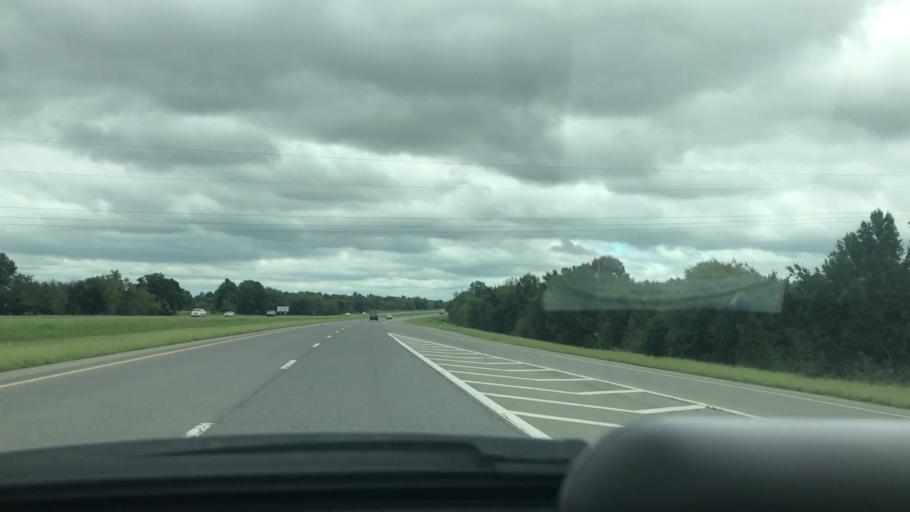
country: US
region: Oklahoma
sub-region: McIntosh County
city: Checotah
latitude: 35.5796
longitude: -95.4908
